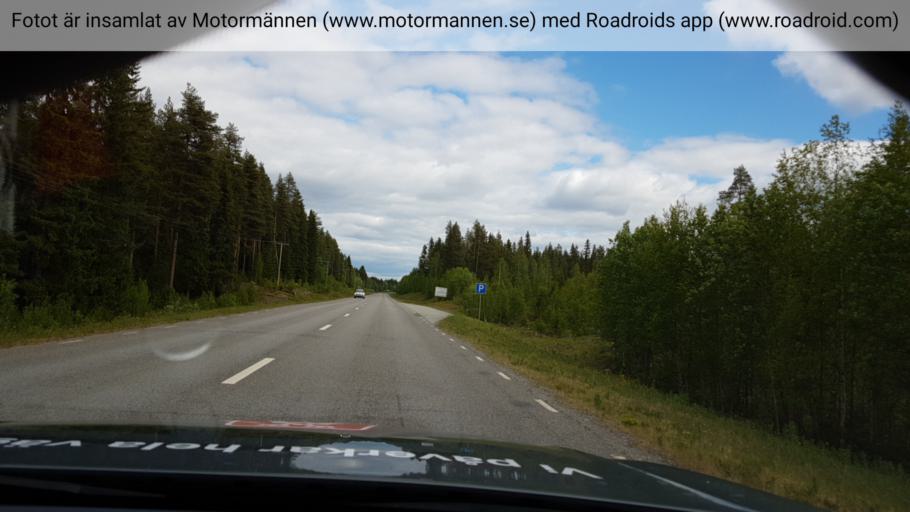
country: SE
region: Jaemtland
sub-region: Stroemsunds Kommun
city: Stroemsund
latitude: 64.2249
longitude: 15.5139
